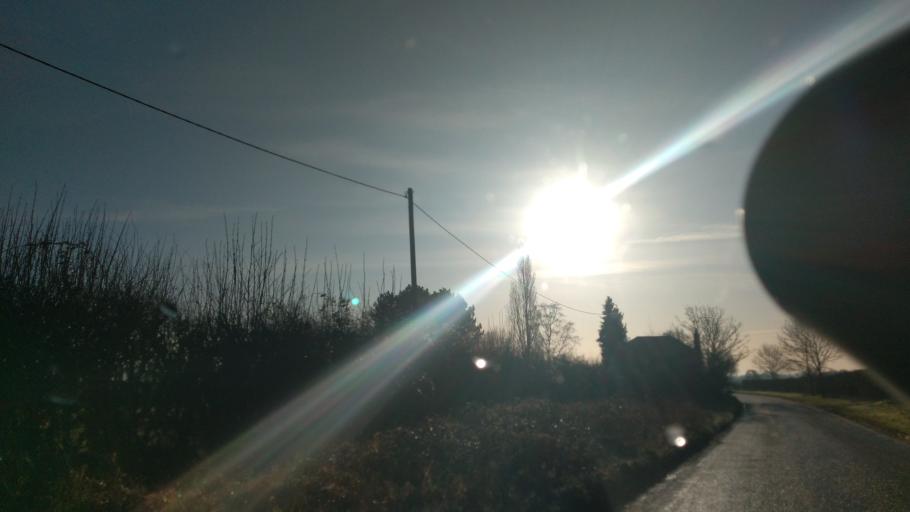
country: GB
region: England
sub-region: Wiltshire
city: Corsham
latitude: 51.4424
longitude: -2.1582
